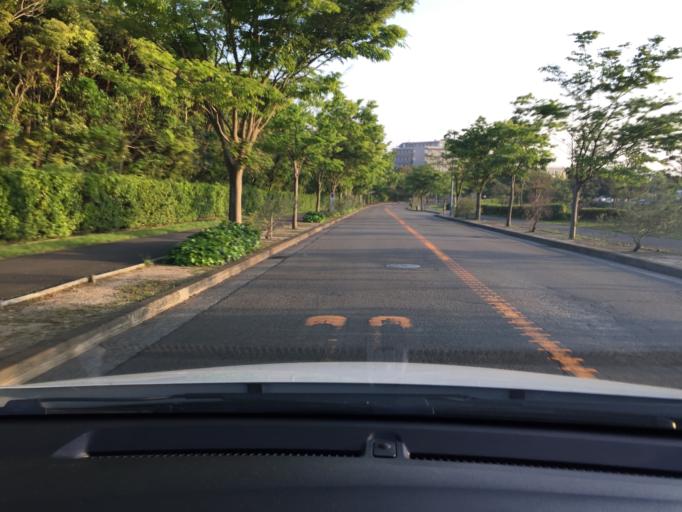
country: JP
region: Kanagawa
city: Hayama
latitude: 35.2589
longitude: 139.6065
